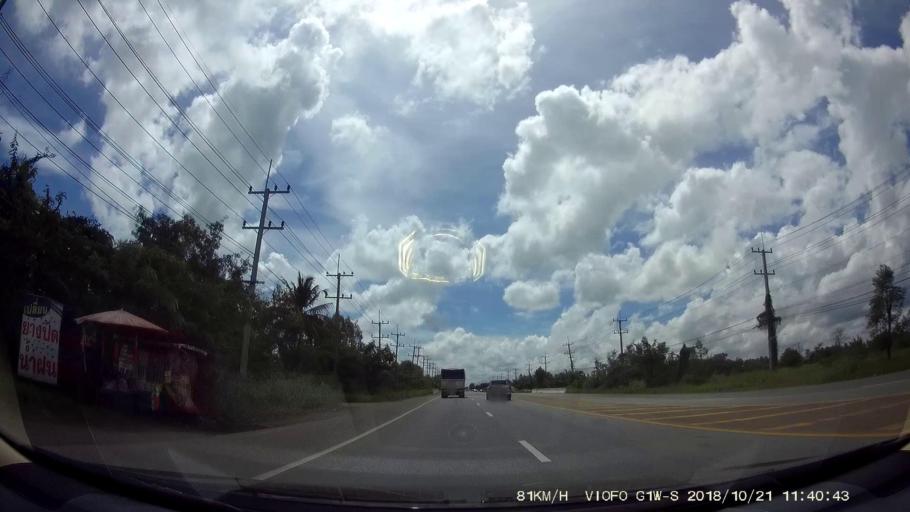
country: TH
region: Chaiyaphum
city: Chaiyaphum
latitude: 15.7097
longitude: 102.0155
